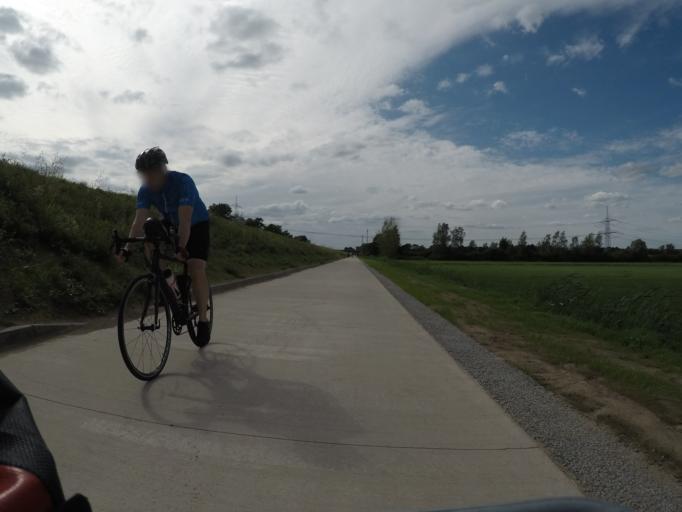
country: DE
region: Lower Saxony
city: Handorf
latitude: 53.3567
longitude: 10.3502
